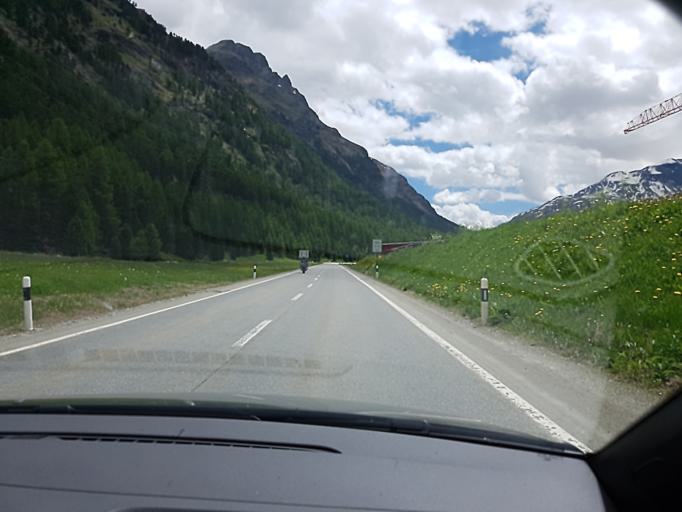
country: CH
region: Grisons
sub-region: Maloja District
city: Pontresina
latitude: 46.4808
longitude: 9.9162
